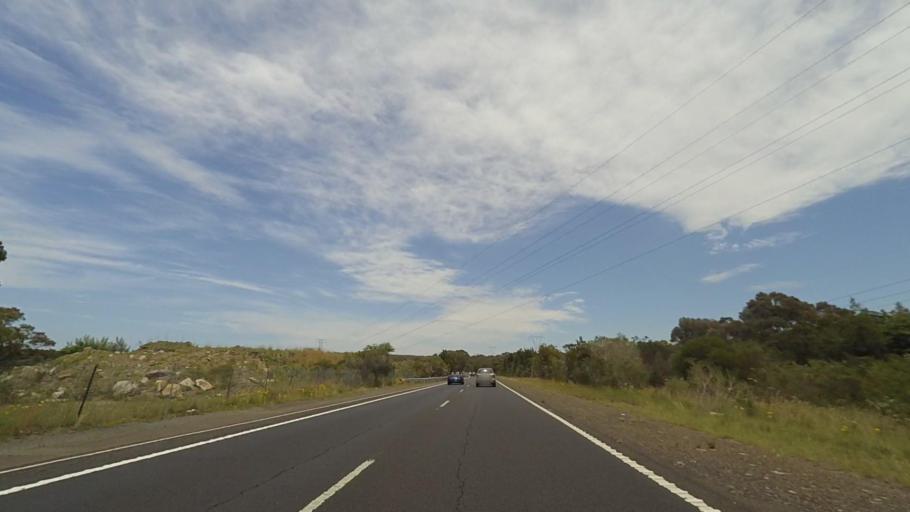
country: AU
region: New South Wales
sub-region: Wollongong
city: Helensburgh
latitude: -34.2252
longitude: 150.9504
